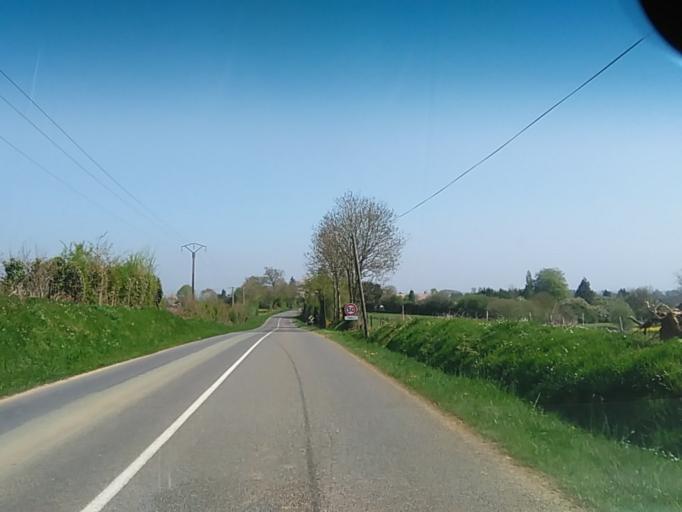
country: FR
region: Lower Normandy
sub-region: Departement de l'Orne
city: Pont-Ecrepin
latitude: 48.7151
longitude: -0.2726
